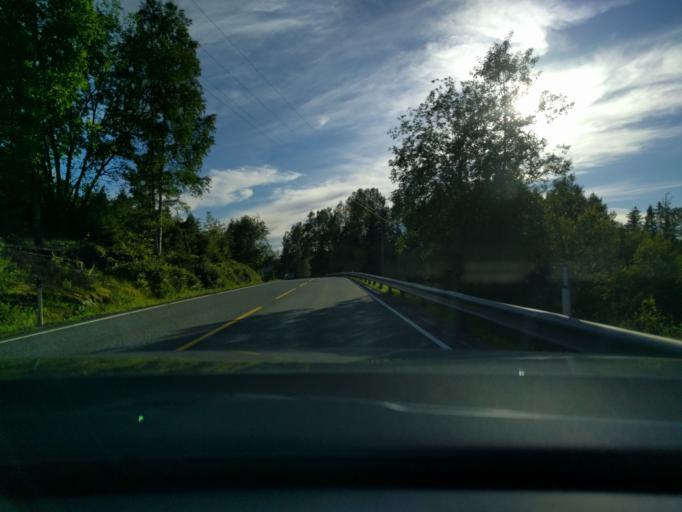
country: NO
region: Vestfold
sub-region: Hof
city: Hof
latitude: 59.5133
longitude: 10.1196
